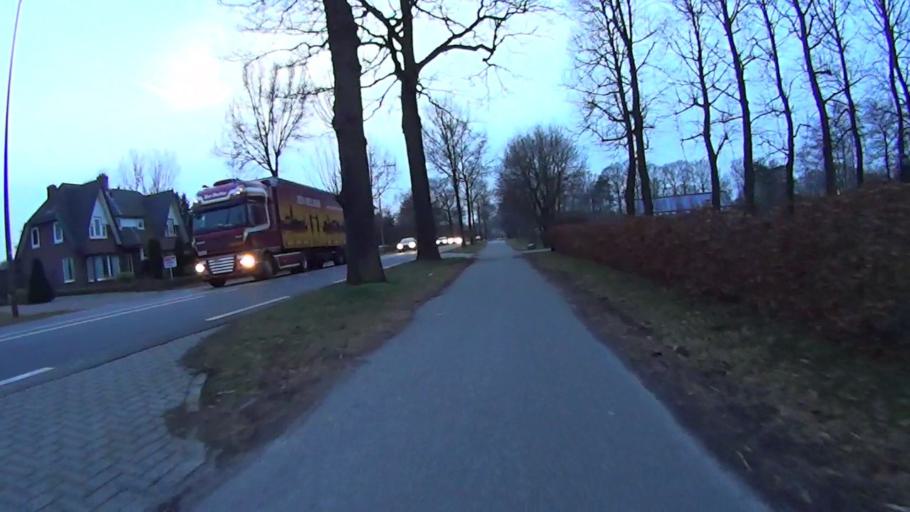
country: NL
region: Utrecht
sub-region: Gemeente Soest
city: Soest
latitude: 52.1607
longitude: 5.3319
